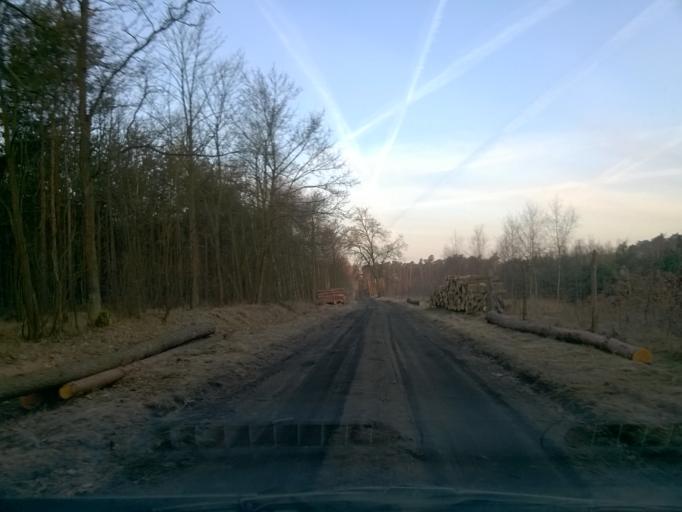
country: PL
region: Kujawsko-Pomorskie
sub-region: Powiat nakielski
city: Sadki
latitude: 53.1219
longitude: 17.4246
